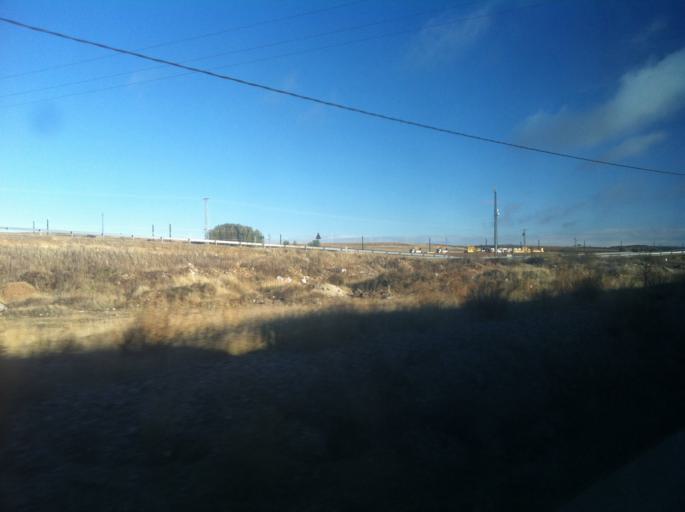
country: ES
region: Castille and Leon
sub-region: Provincia de Palencia
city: Villodrigo
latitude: 42.1404
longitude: -4.1179
